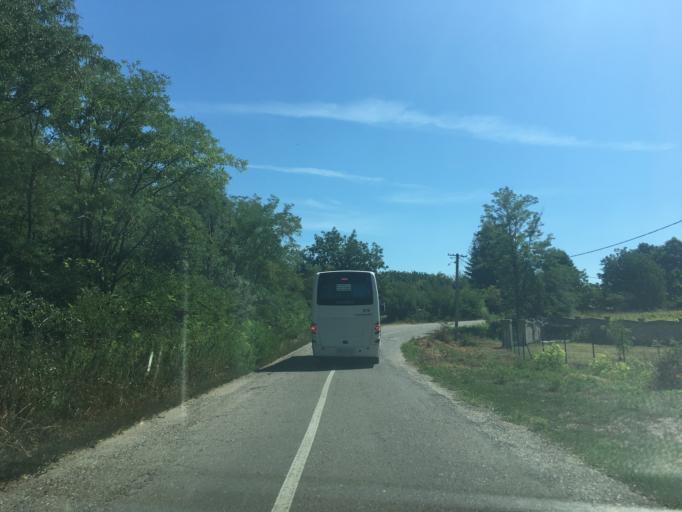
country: RS
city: Vladimirovac
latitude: 45.0013
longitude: 20.9420
